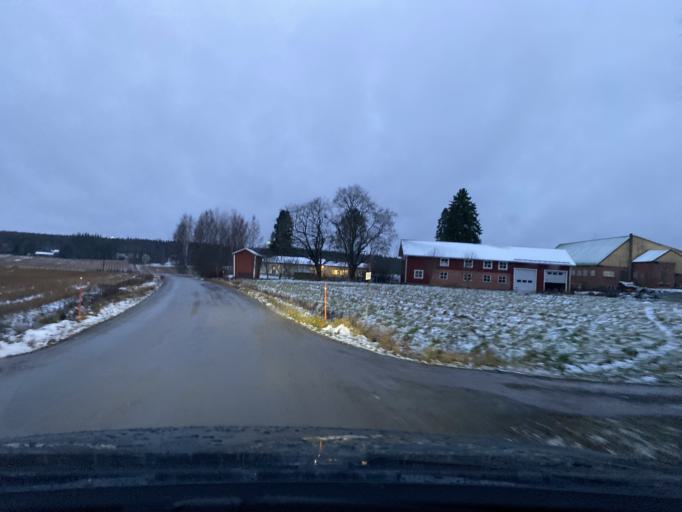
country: FI
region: Pirkanmaa
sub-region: Lounais-Pirkanmaa
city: Punkalaidun
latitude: 61.1400
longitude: 22.9634
